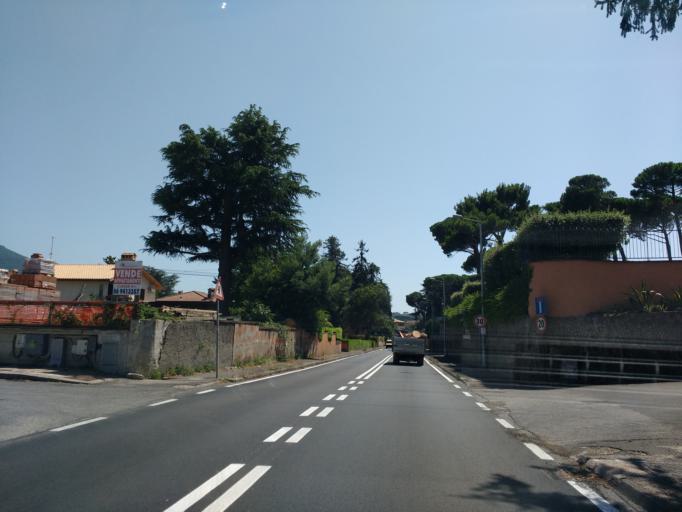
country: IT
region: Latium
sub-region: Citta metropolitana di Roma Capitale
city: Grottaferrata
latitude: 41.7874
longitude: 12.6818
